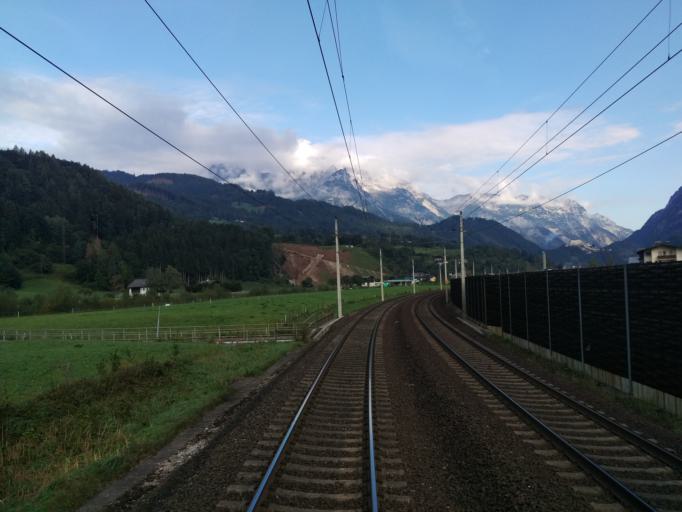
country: AT
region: Salzburg
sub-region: Politischer Bezirk Sankt Johann im Pongau
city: Pfarrwerfen
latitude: 47.4566
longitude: 13.2030
